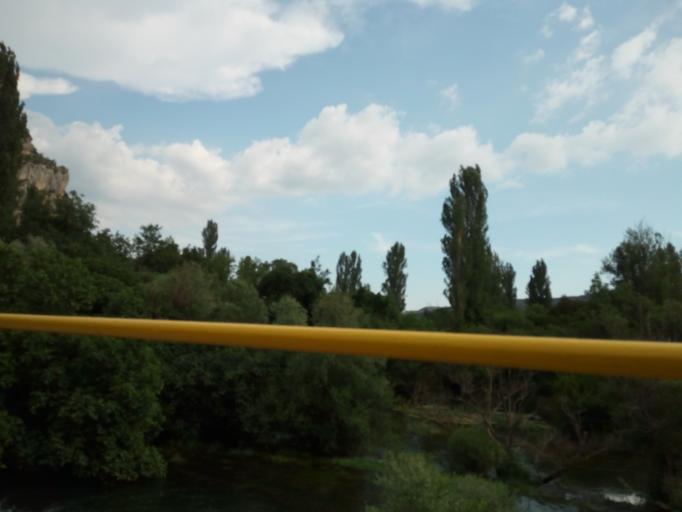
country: HR
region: Sibensko-Kniniska
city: Kistanje
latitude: 43.9062
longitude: 15.9750
